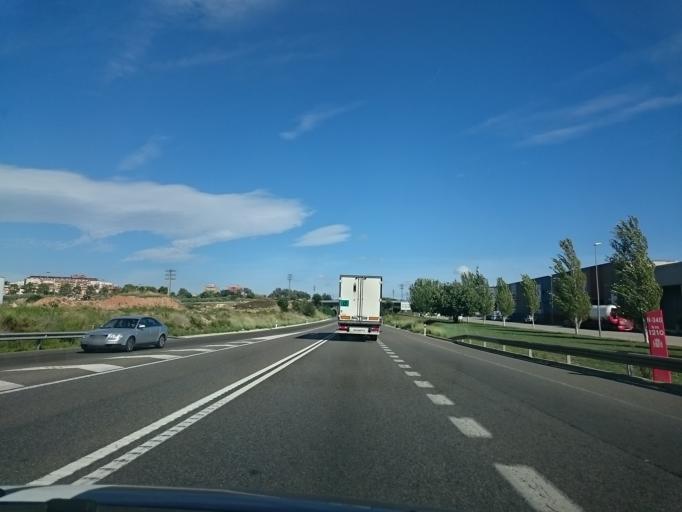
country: ES
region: Catalonia
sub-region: Provincia de Barcelona
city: Vilafranca del Penedes
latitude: 41.3342
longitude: 1.6881
